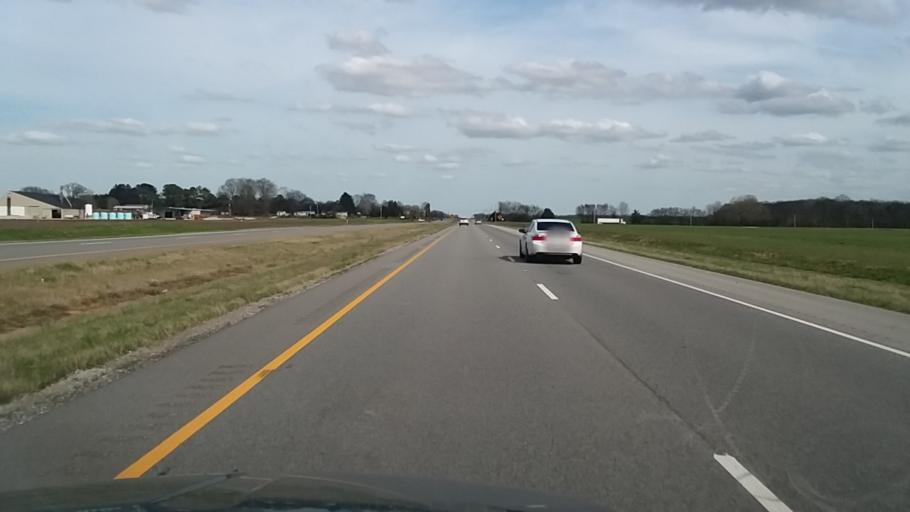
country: US
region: Alabama
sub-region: Colbert County
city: Muscle Shoals
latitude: 34.6848
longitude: -87.5704
